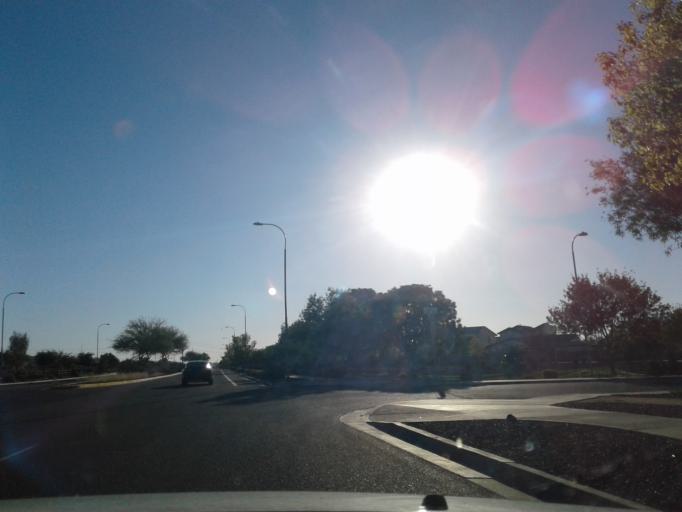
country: US
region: Arizona
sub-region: Maricopa County
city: Laveen
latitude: 33.3774
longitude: -112.2130
